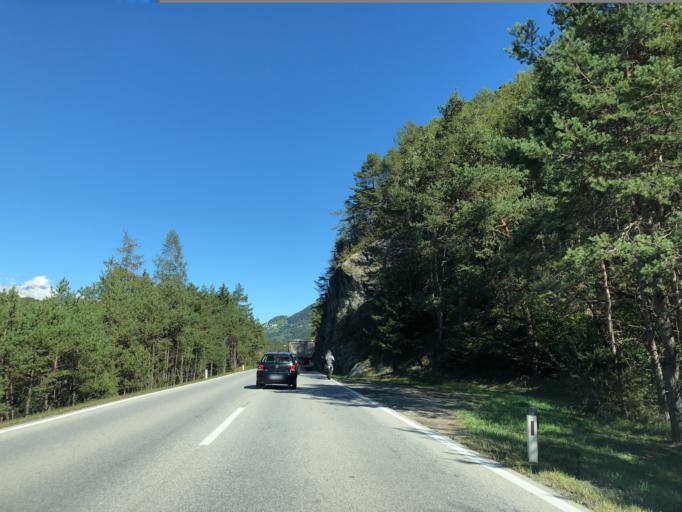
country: AT
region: Tyrol
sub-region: Politischer Bezirk Imst
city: Roppen
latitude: 47.2223
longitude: 10.8374
